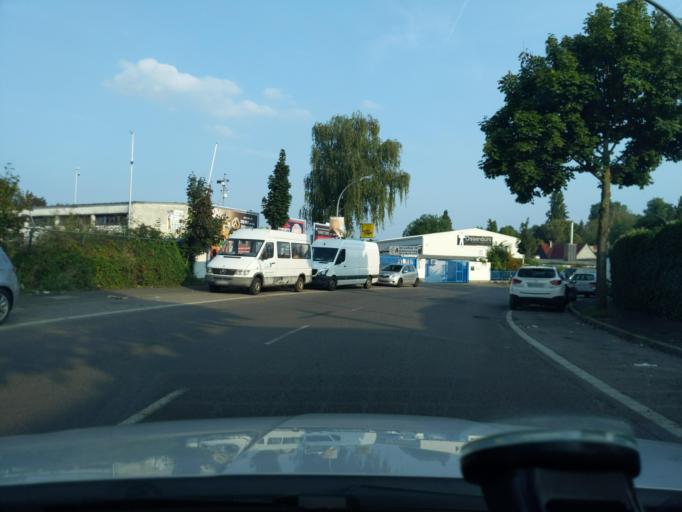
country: DE
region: North Rhine-Westphalia
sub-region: Regierungsbezirk Dusseldorf
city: Dusseldorf
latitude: 51.2095
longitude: 6.8140
